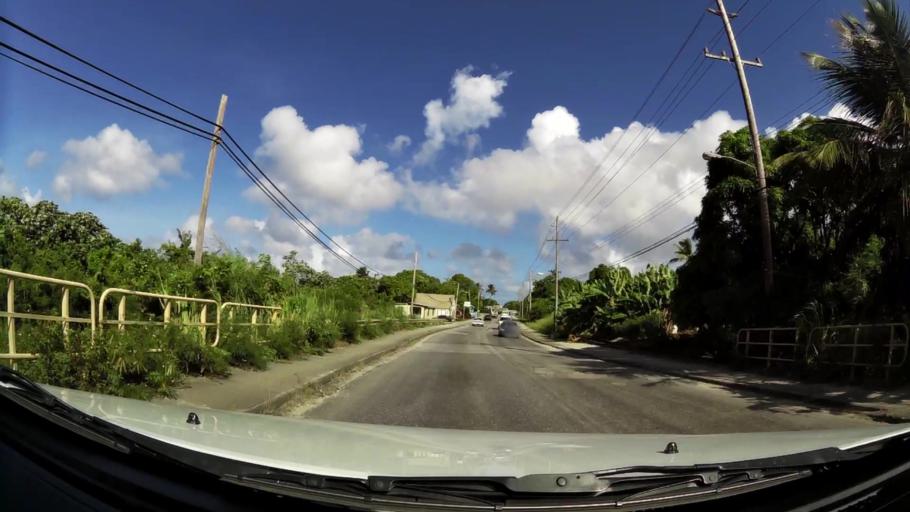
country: BB
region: Saint James
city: Holetown
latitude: 13.2182
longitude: -59.6209
